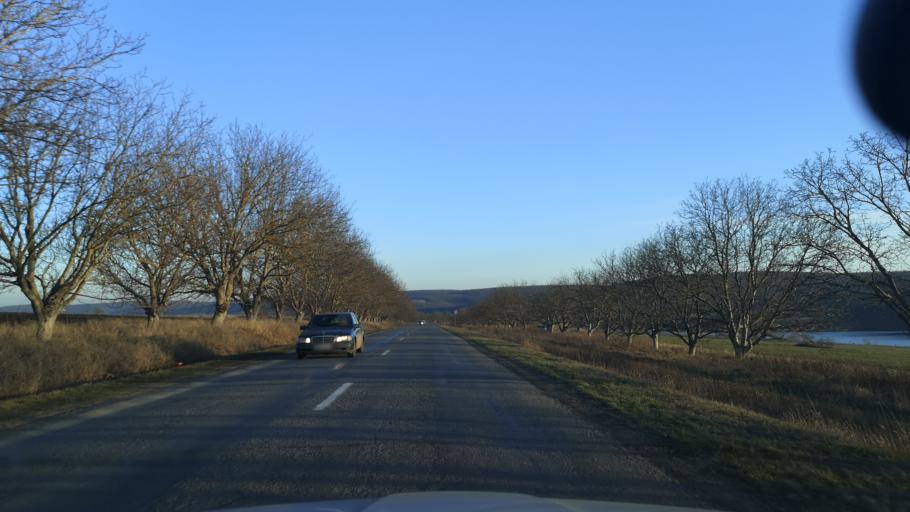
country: MD
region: Orhei
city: Orhei
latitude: 47.2878
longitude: 28.8207
